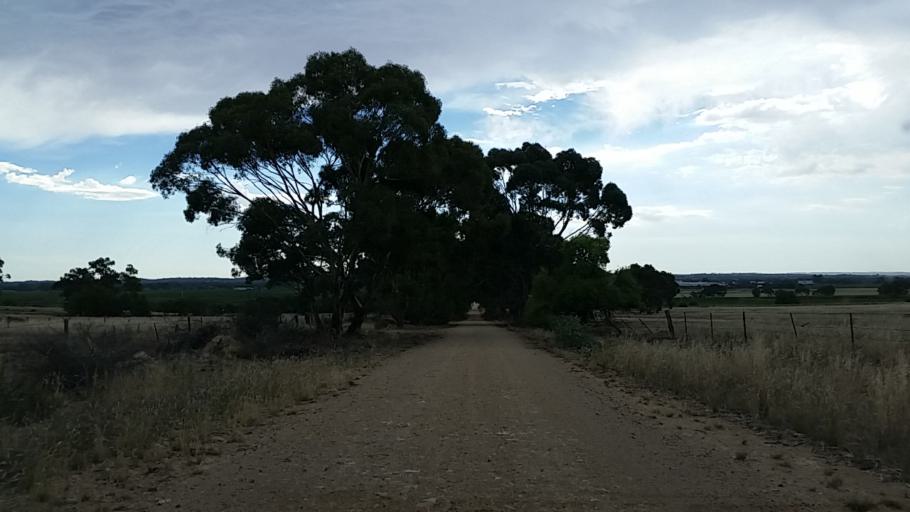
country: AU
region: South Australia
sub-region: Barossa
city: Angaston
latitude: -34.4517
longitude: 139.0546
